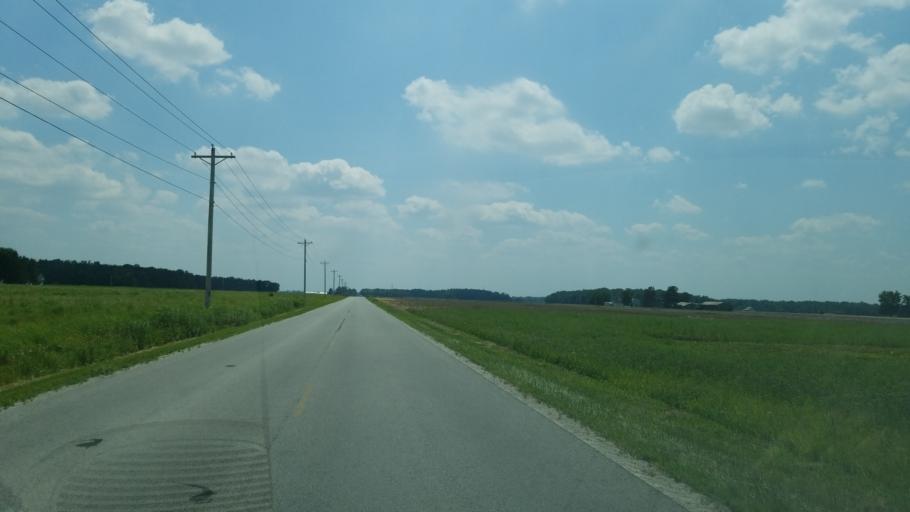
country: US
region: Ohio
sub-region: Wood County
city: North Baltimore
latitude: 41.2361
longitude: -83.5542
